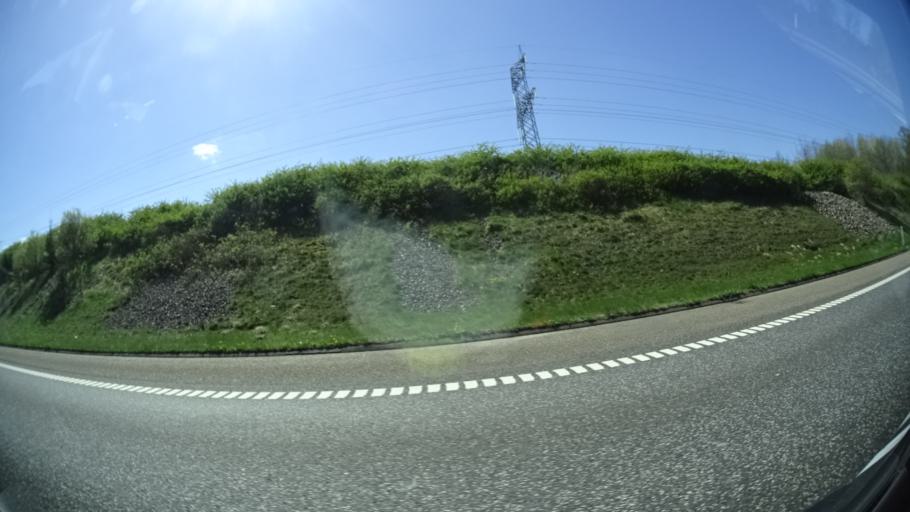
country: DK
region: Central Jutland
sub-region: Arhus Kommune
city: Trige
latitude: 56.2965
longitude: 10.1308
